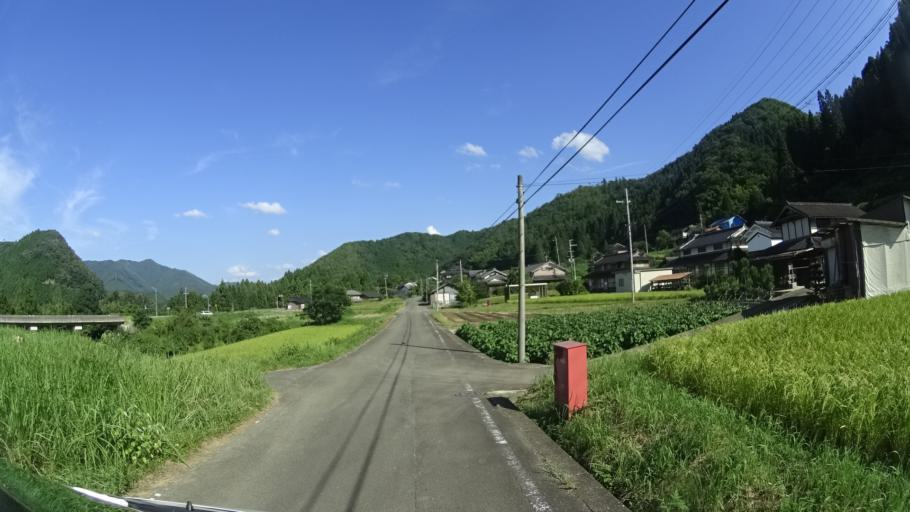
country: JP
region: Kyoto
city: Ayabe
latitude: 35.2690
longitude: 135.3638
